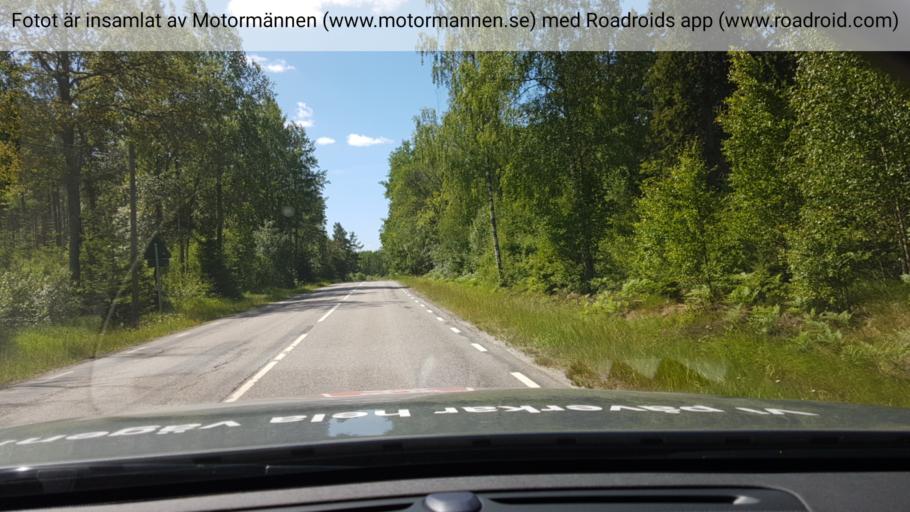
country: SE
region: Stockholm
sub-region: Haninge Kommun
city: Haninge
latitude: 59.1247
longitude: 18.1892
